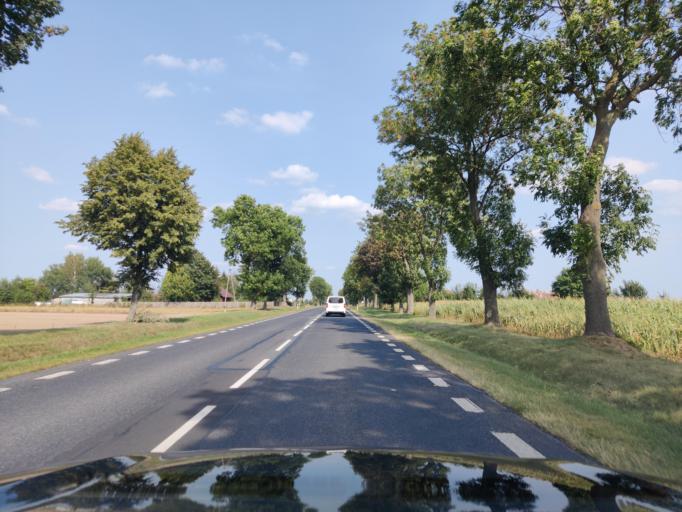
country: PL
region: Masovian Voivodeship
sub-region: Powiat makowski
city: Rzewnie
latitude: 52.8624
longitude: 21.3203
